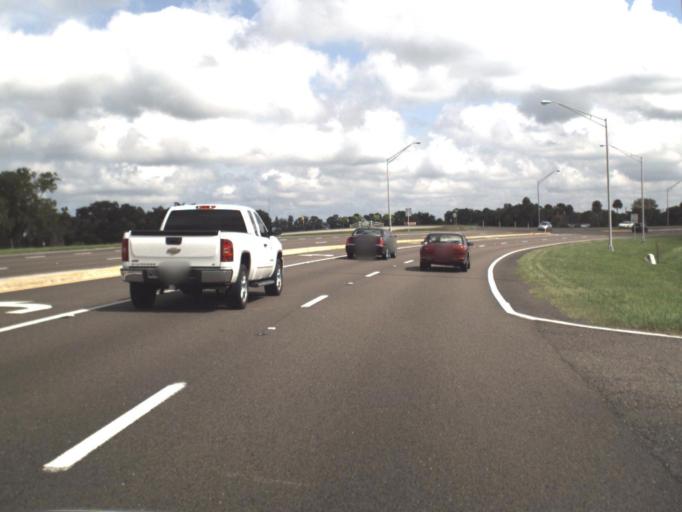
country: US
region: Florida
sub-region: Manatee County
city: Palmetto
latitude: 27.5323
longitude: -82.5727
